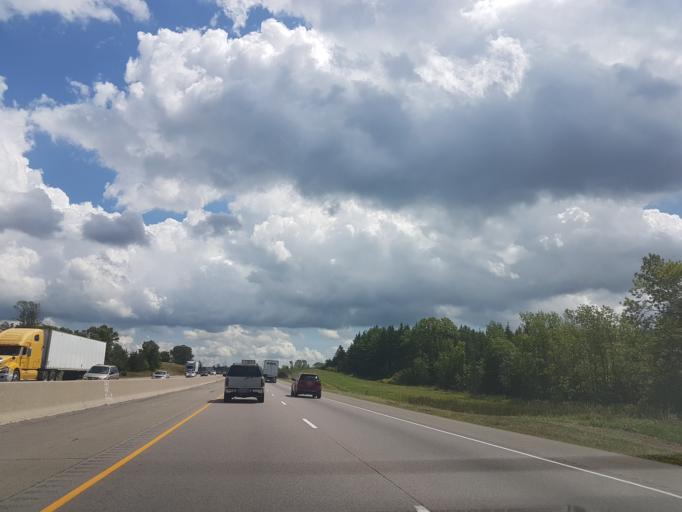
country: CA
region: Ontario
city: Belleville
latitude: 44.2199
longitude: -77.2752
